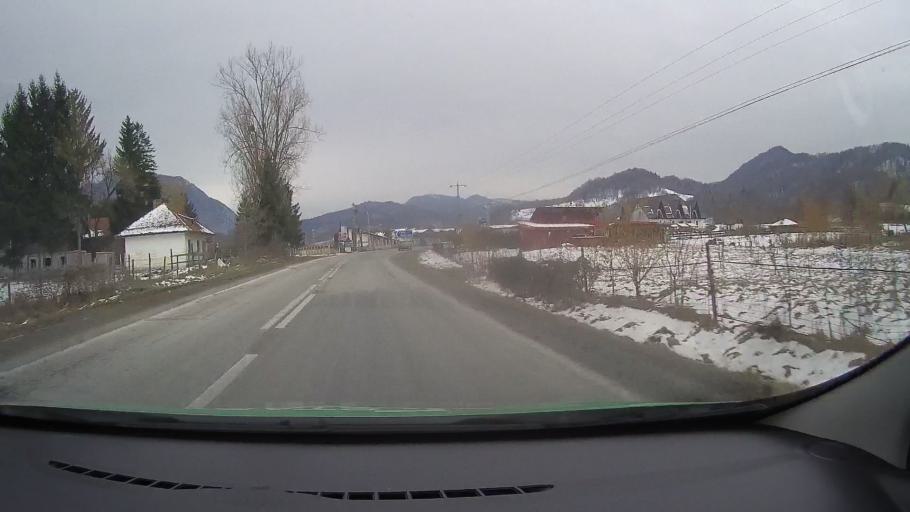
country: RO
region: Brasov
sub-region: Oras Rasnov
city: Rasnov
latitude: 45.5544
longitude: 25.4862
